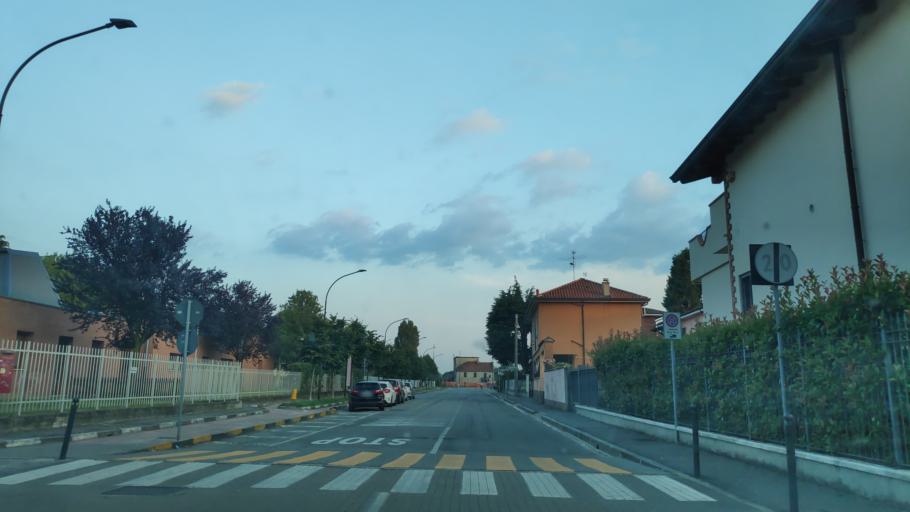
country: IT
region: Lombardy
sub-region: Citta metropolitana di Milano
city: Melzo
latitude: 45.4950
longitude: 9.4258
